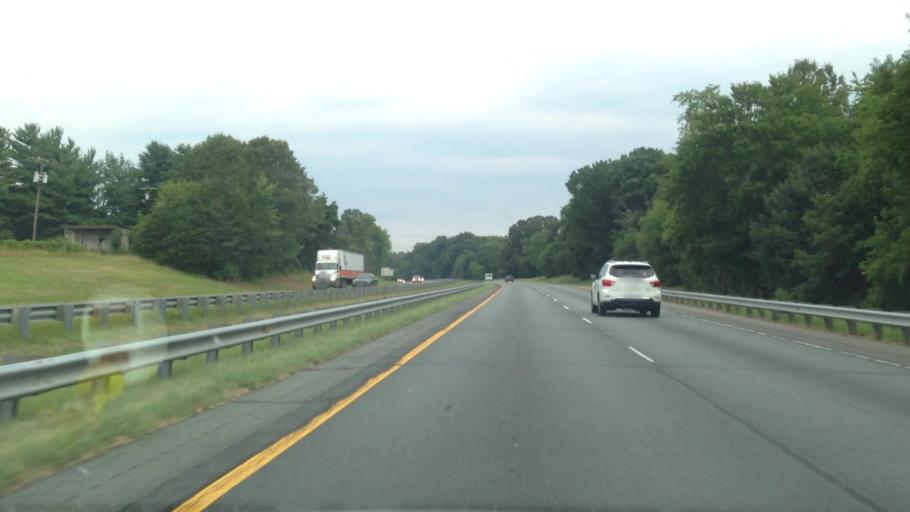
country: US
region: North Carolina
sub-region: Stokes County
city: King
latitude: 36.2737
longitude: -80.3782
